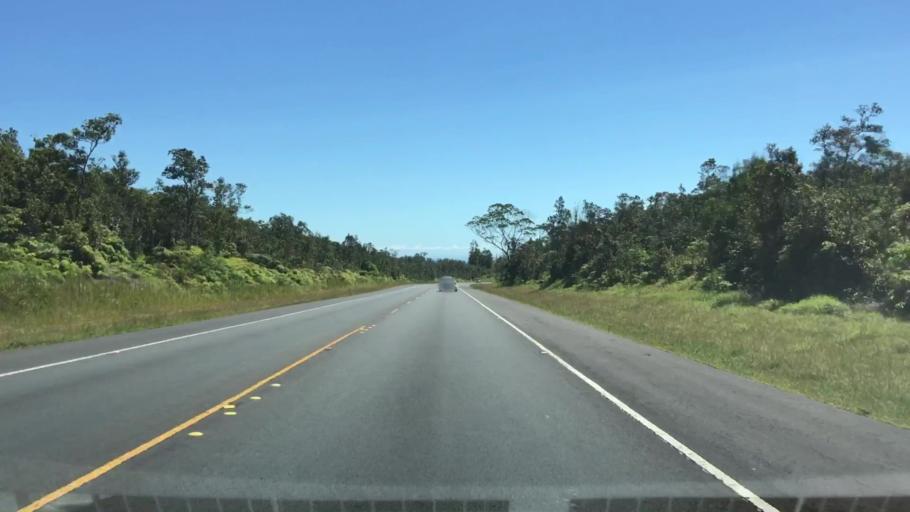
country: US
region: Hawaii
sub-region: Hawaii County
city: Volcano
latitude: 19.4481
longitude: -155.2012
